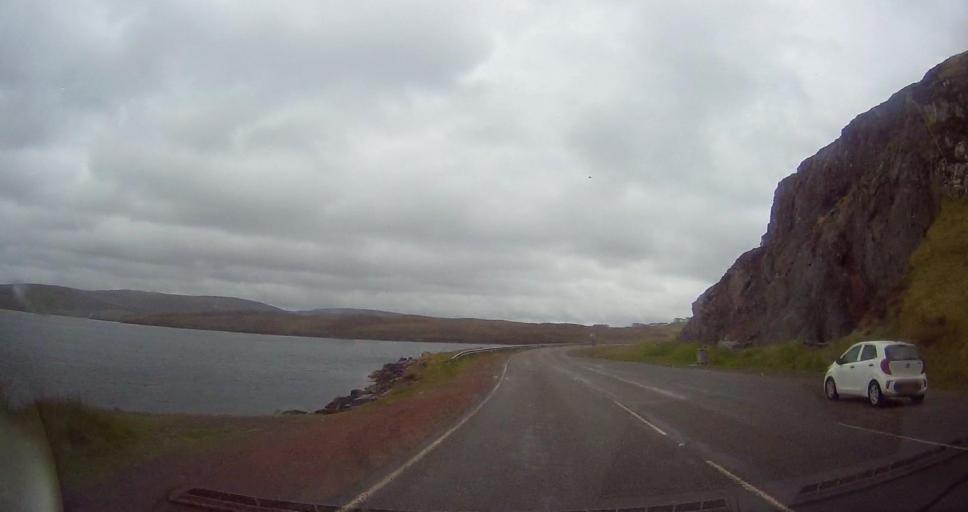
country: GB
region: Scotland
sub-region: Shetland Islands
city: Lerwick
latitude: 60.3977
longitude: -1.3847
